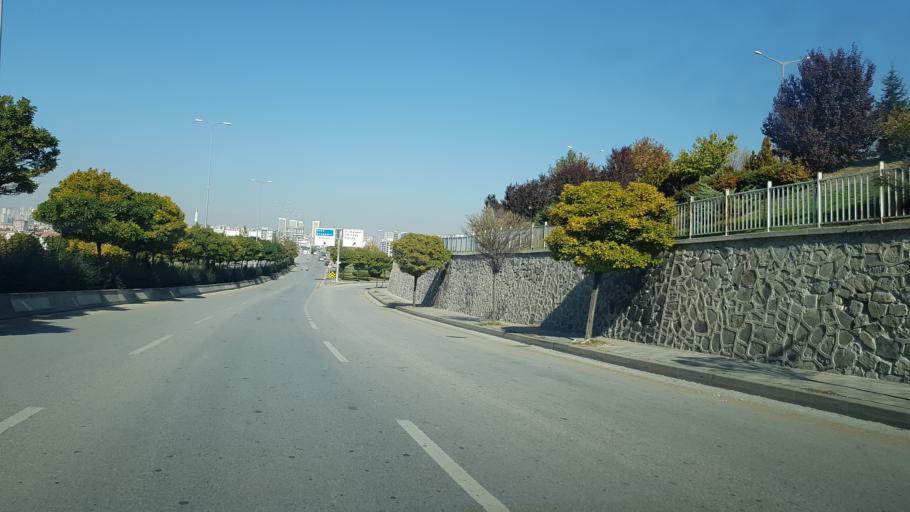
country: TR
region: Ankara
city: Etimesgut
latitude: 39.9572
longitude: 32.6049
